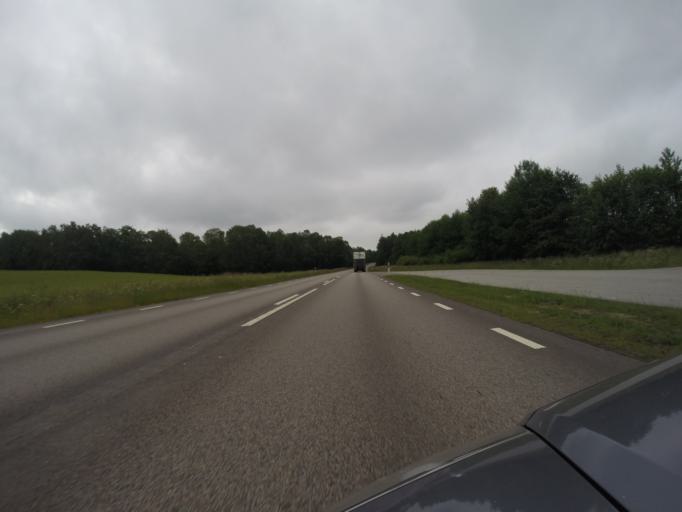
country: SE
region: Skane
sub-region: Bjuvs Kommun
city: Billesholm
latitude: 56.0416
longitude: 12.9694
